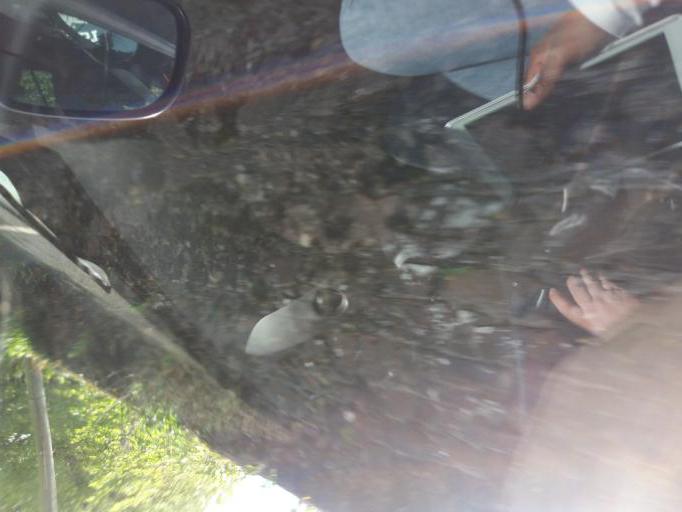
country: IE
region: Munster
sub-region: Waterford
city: Dunmore East
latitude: 52.2418
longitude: -6.9483
